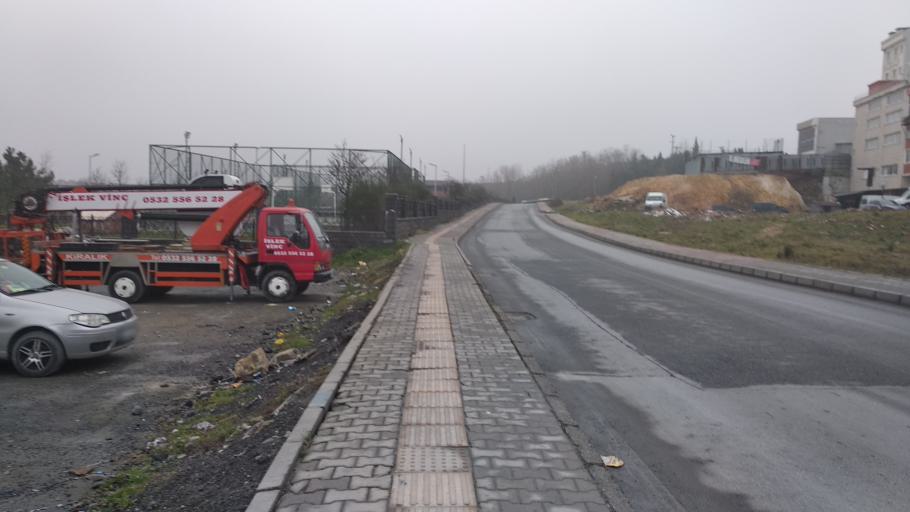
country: TR
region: Istanbul
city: Basaksehir
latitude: 41.1801
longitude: 28.7469
